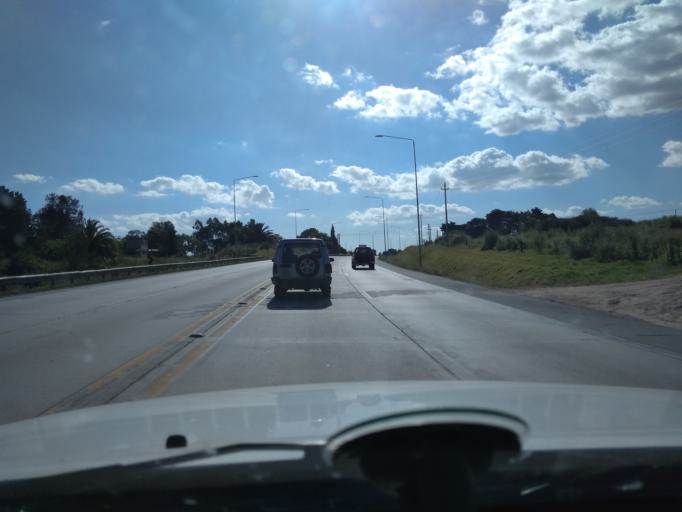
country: UY
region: Canelones
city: La Paz
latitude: -34.7831
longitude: -56.2475
